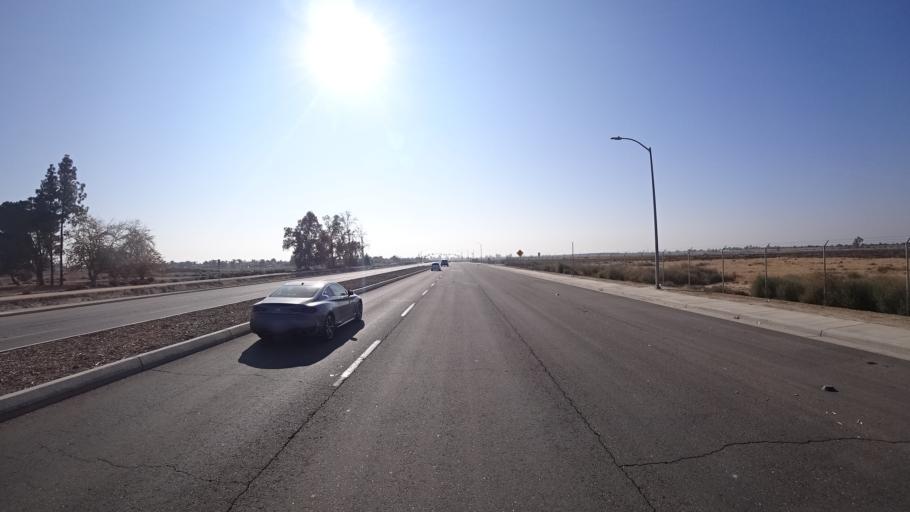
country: US
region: California
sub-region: Kern County
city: Greenfield
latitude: 35.2914
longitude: -119.0214
